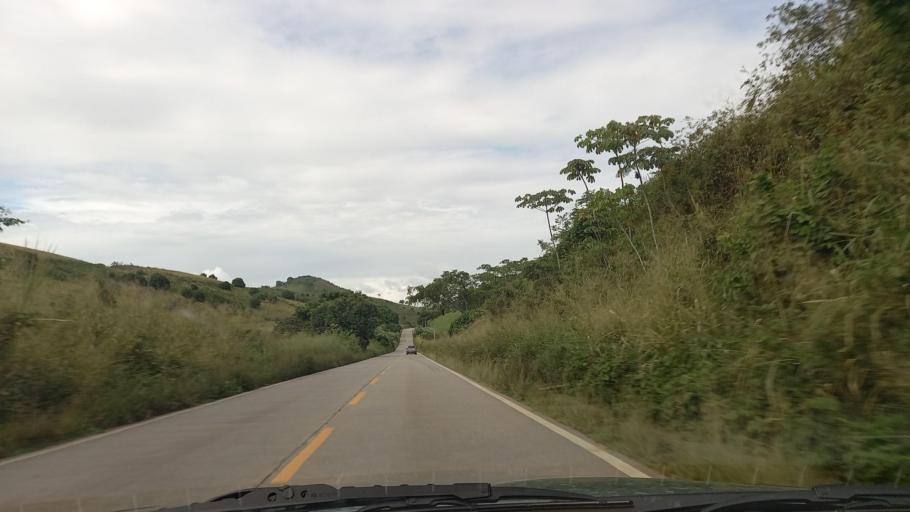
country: BR
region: Pernambuco
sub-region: Catende
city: Catende
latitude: -8.6972
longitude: -35.7344
